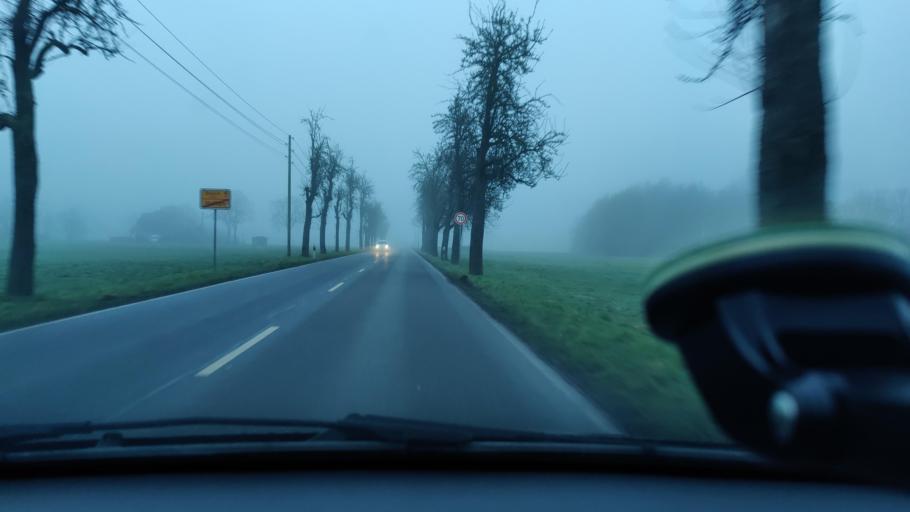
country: DE
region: North Rhine-Westphalia
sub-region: Regierungsbezirk Dusseldorf
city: Mehrhoog
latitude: 51.7317
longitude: 6.4614
